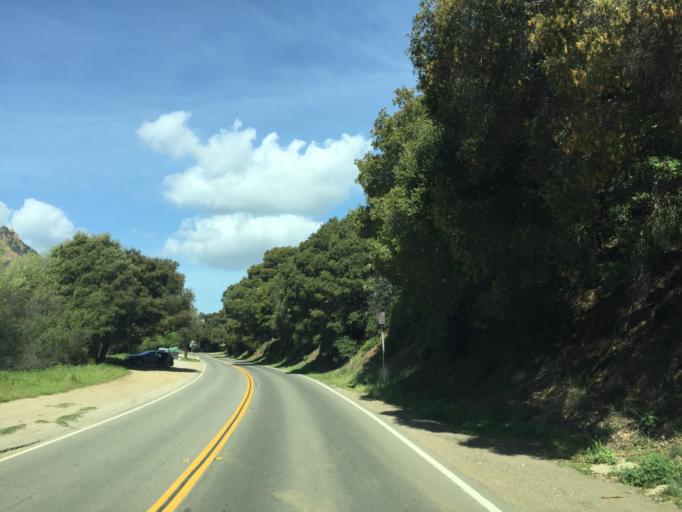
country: US
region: California
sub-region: Los Angeles County
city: Malibu Beach
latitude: 34.0811
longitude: -118.7019
